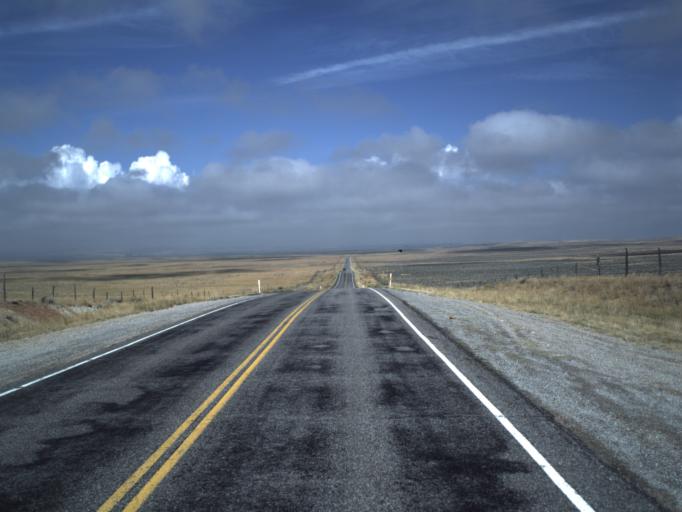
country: US
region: Wyoming
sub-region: Uinta County
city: Evanston
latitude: 41.4436
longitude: -111.0771
